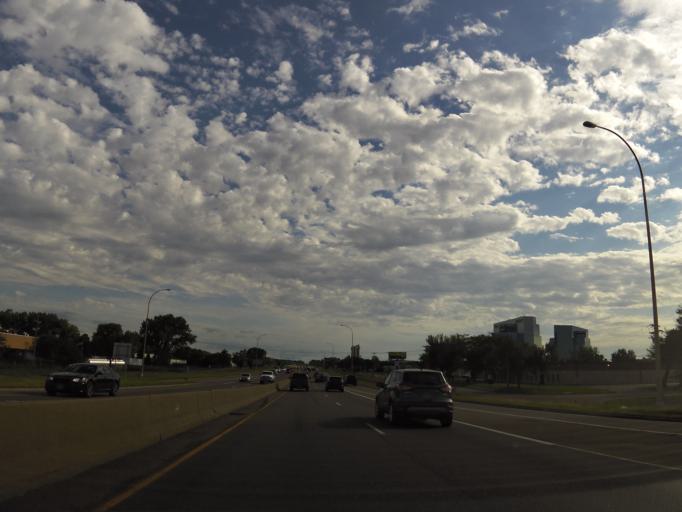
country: US
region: Minnesota
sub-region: Hennepin County
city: New Hope
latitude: 44.9902
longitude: -93.4009
